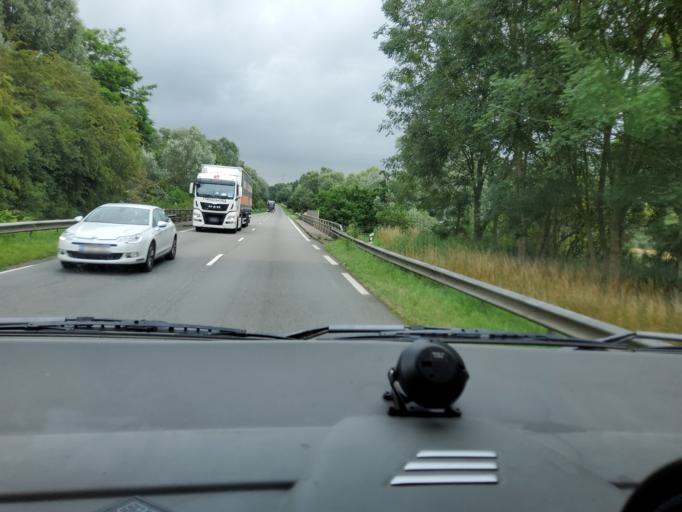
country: FR
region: Nord-Pas-de-Calais
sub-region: Departement du Nord
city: Watten
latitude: 50.8350
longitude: 2.2006
